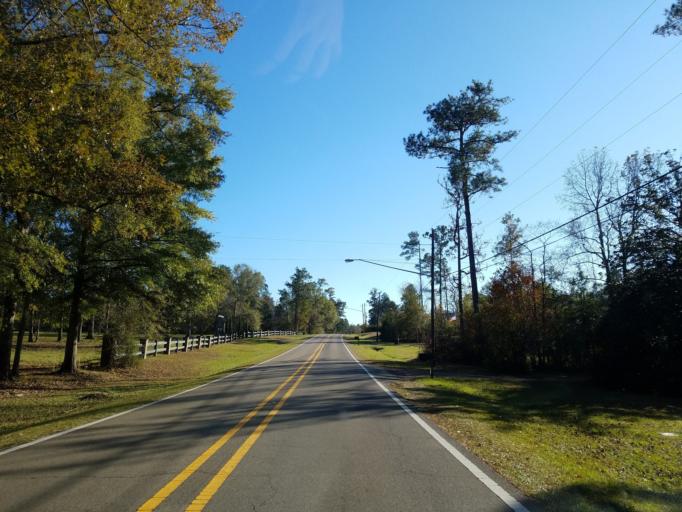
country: US
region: Mississippi
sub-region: Forrest County
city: Hattiesburg
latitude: 31.2656
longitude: -89.2927
